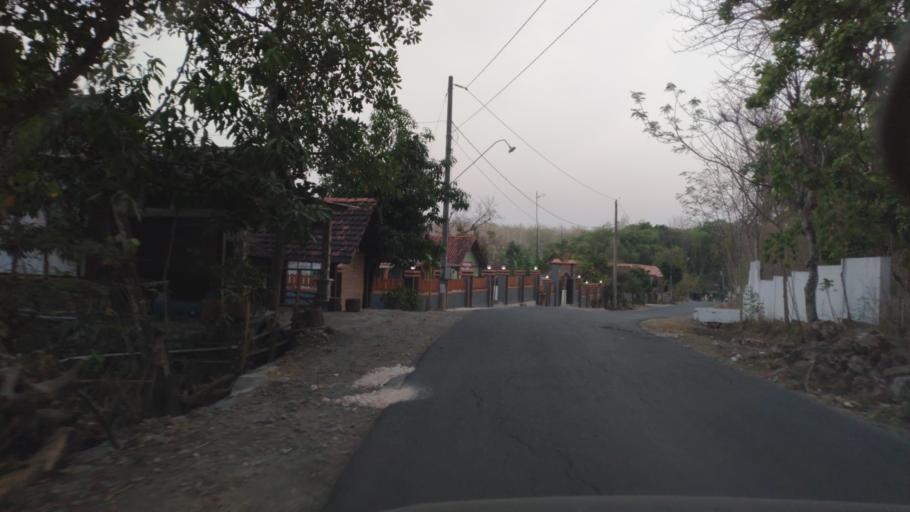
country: ID
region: Central Java
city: Ngliron
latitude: -7.1053
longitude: 111.4245
